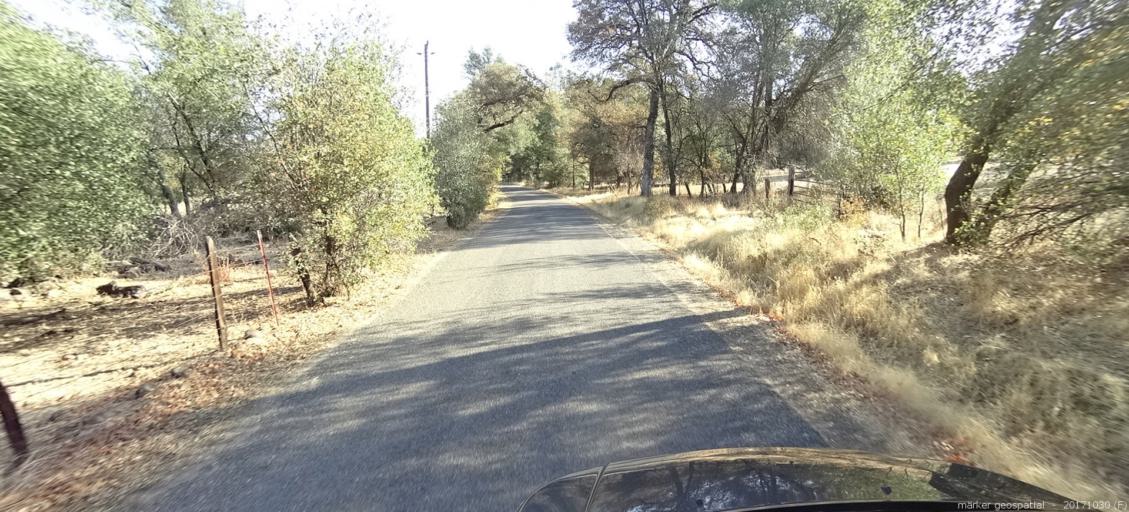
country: US
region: California
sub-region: Shasta County
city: Palo Cedro
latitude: 40.5658
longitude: -122.1454
